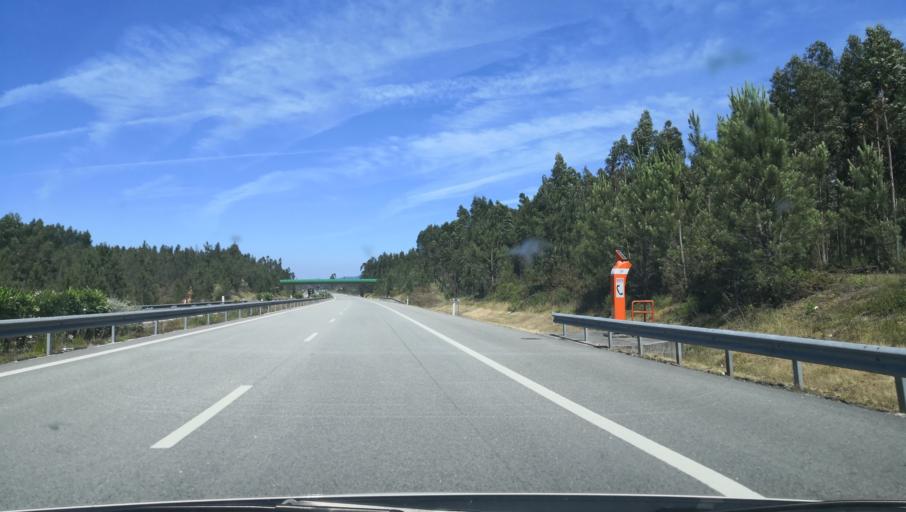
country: PT
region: Coimbra
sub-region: Montemor-O-Velho
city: Arazede
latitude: 40.2757
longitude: -8.5933
